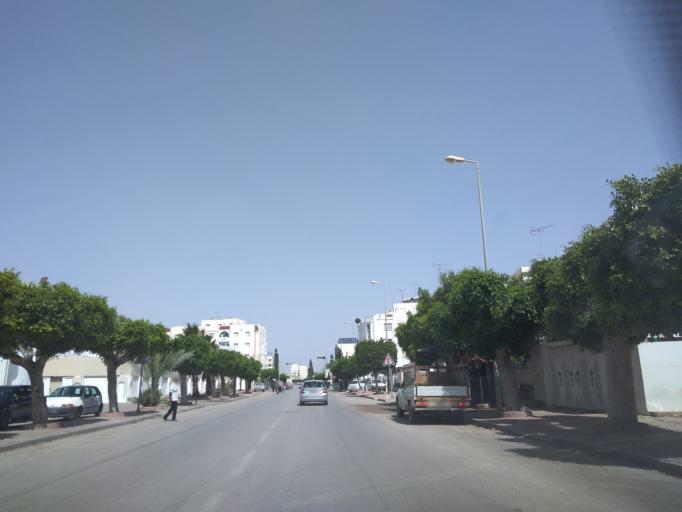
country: TN
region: Safaqis
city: Sfax
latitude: 34.7420
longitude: 10.7508
